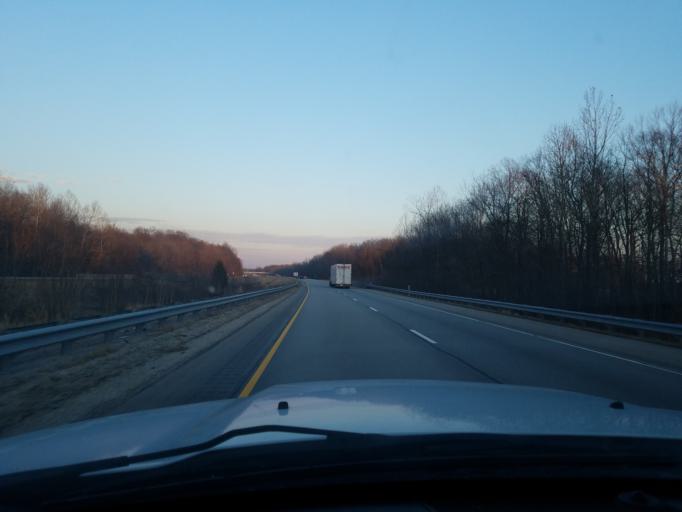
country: US
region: Indiana
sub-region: Warrick County
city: Chandler
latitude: 38.1842
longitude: -87.3657
